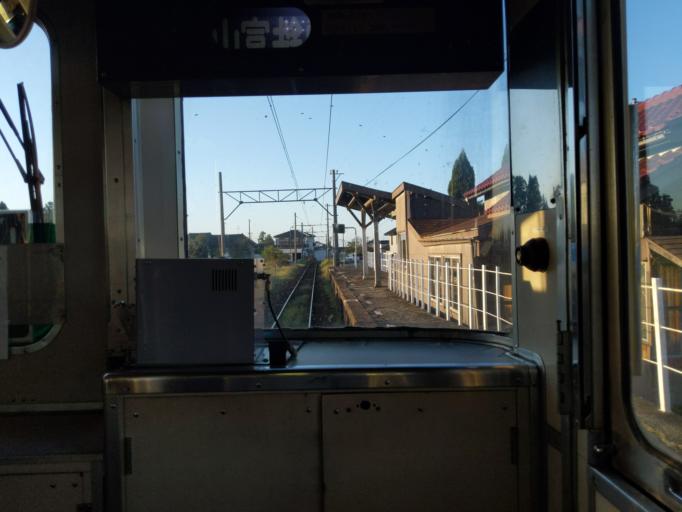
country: JP
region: Toyama
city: Kamiichi
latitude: 36.6343
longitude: 137.3194
